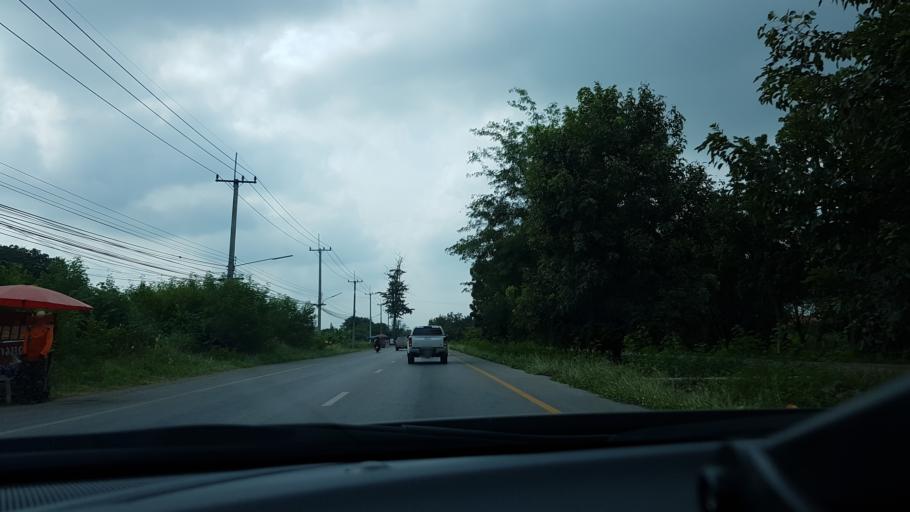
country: TH
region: Phetchabun
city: Si Thep
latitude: 15.5285
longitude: 101.0490
